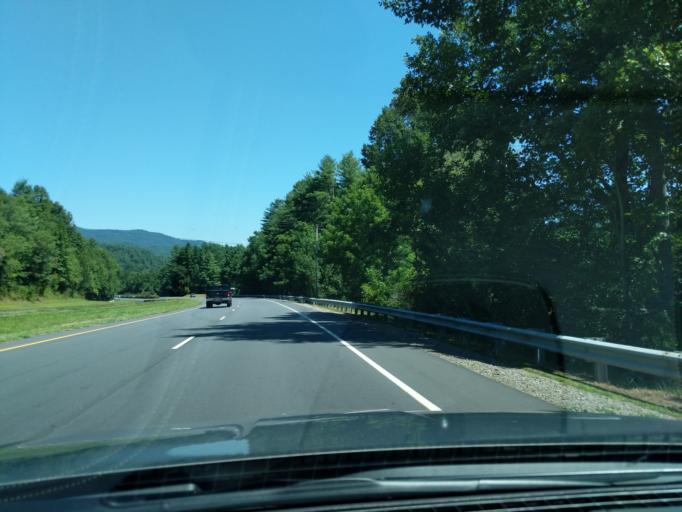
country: US
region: North Carolina
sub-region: Macon County
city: Franklin
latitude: 35.1474
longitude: -83.4696
